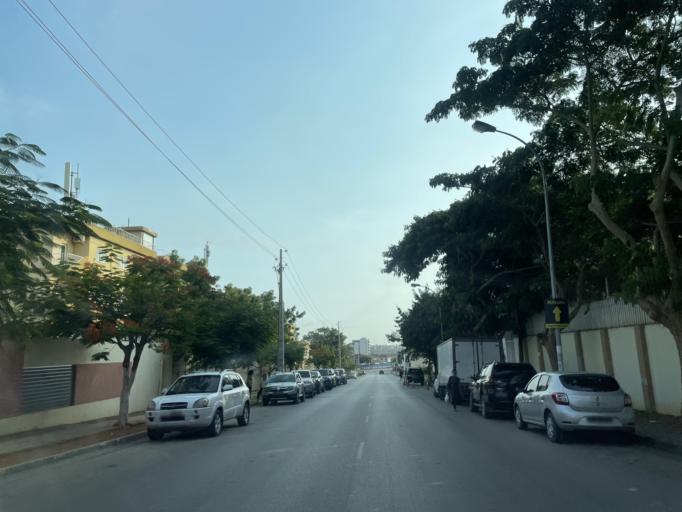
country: AO
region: Luanda
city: Luanda
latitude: -8.9206
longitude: 13.1966
